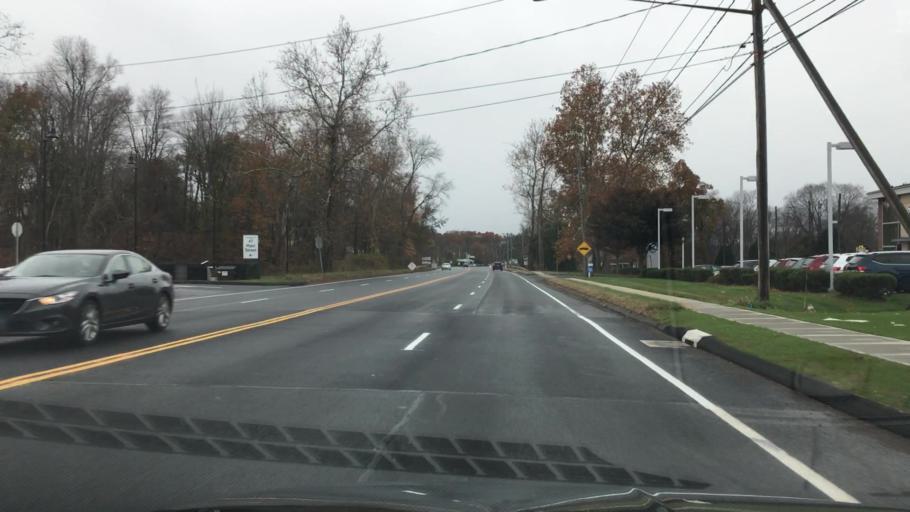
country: US
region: Connecticut
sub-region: Hartford County
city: Manchester
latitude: 41.8212
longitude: -72.5008
